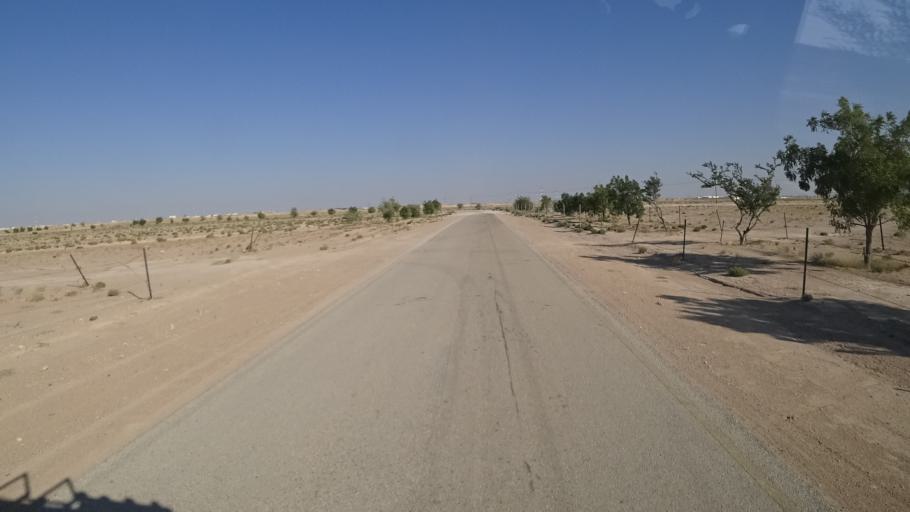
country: OM
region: Zufar
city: Salalah
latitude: 17.5948
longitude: 54.0304
